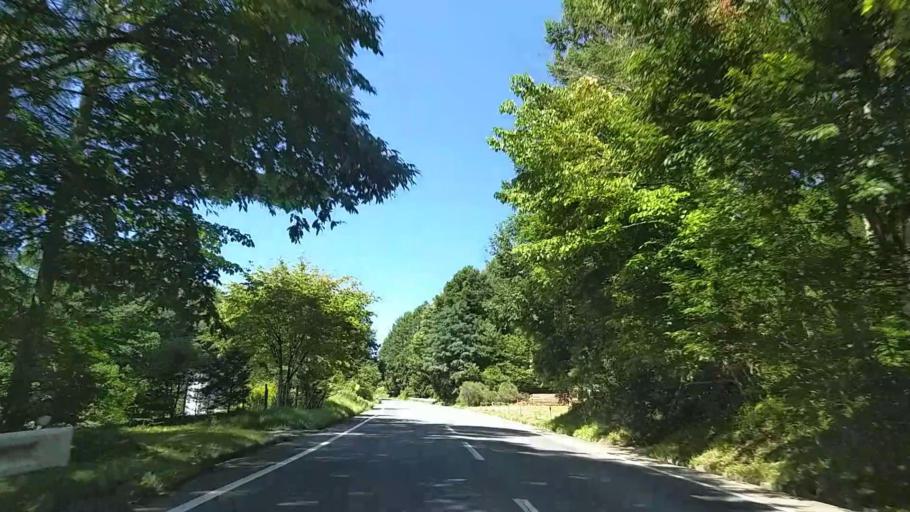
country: JP
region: Nagano
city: Komoro
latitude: 36.3427
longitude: 138.4925
